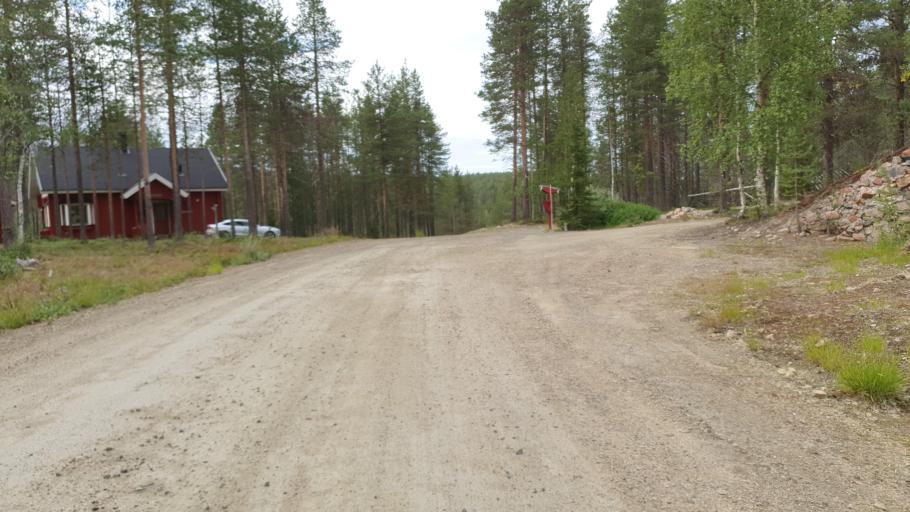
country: FI
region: Lapland
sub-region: Tunturi-Lappi
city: Kolari
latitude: 67.5995
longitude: 24.1360
